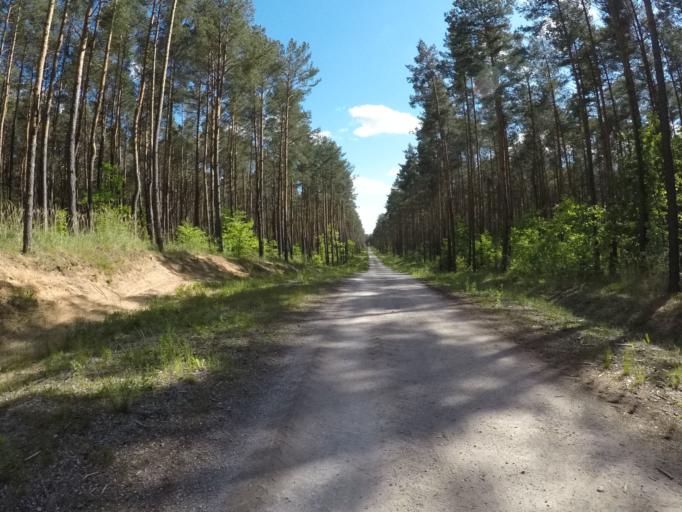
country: PL
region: Swietokrzyskie
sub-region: Powiat kielecki
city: Miedziana Gora
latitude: 50.9023
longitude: 20.5305
